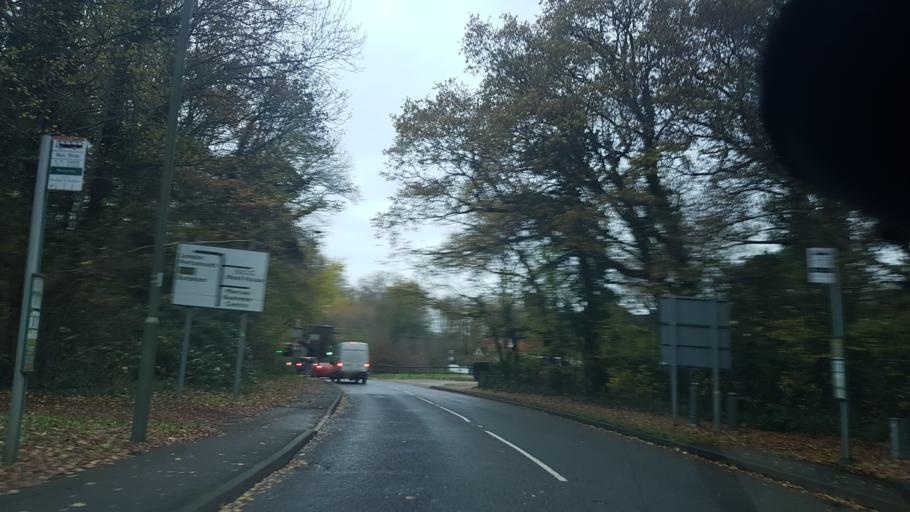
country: GB
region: England
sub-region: Surrey
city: Send
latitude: 51.2559
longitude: -0.5340
